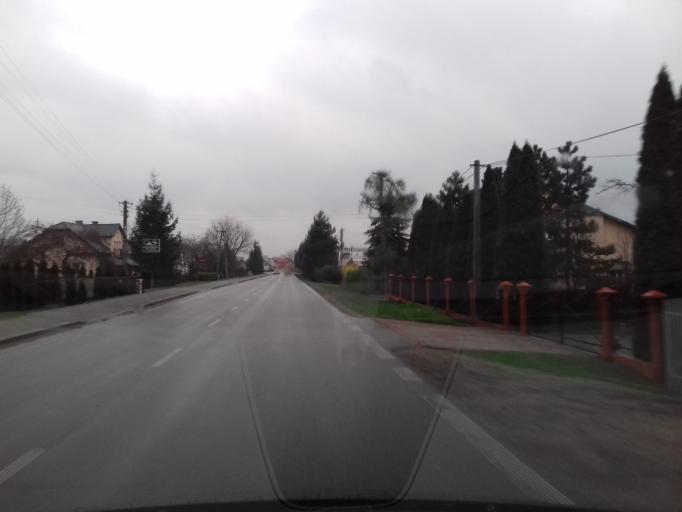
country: PL
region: Lesser Poland Voivodeship
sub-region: Powiat nowosadecki
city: Stary Sacz
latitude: 49.5954
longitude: 20.6337
